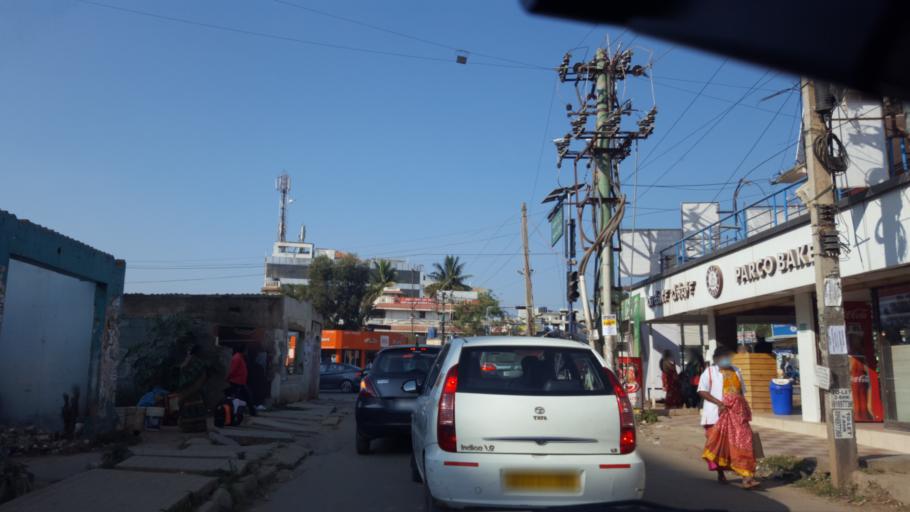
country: IN
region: Karnataka
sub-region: Bangalore Urban
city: Bangalore
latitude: 12.9554
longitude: 77.7147
